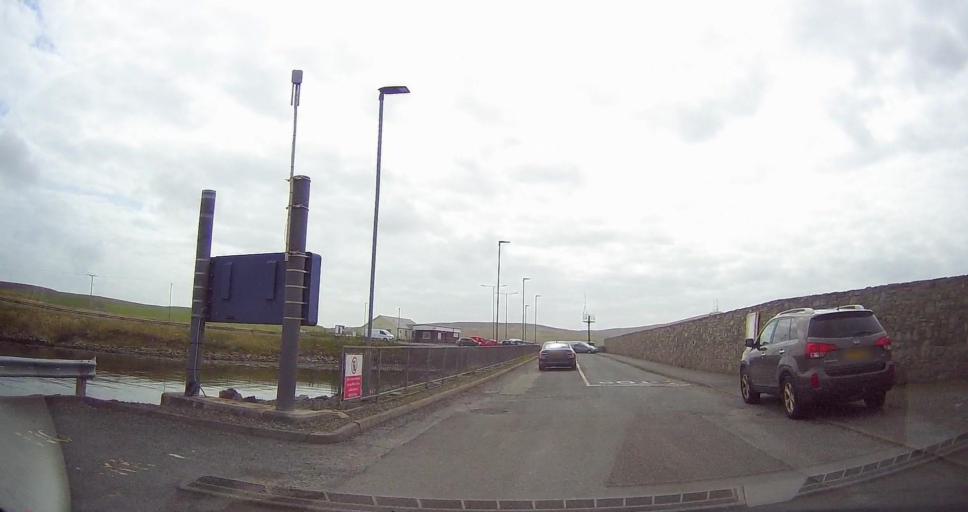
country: GB
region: Scotland
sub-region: Shetland Islands
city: Shetland
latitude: 60.1569
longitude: -1.1230
